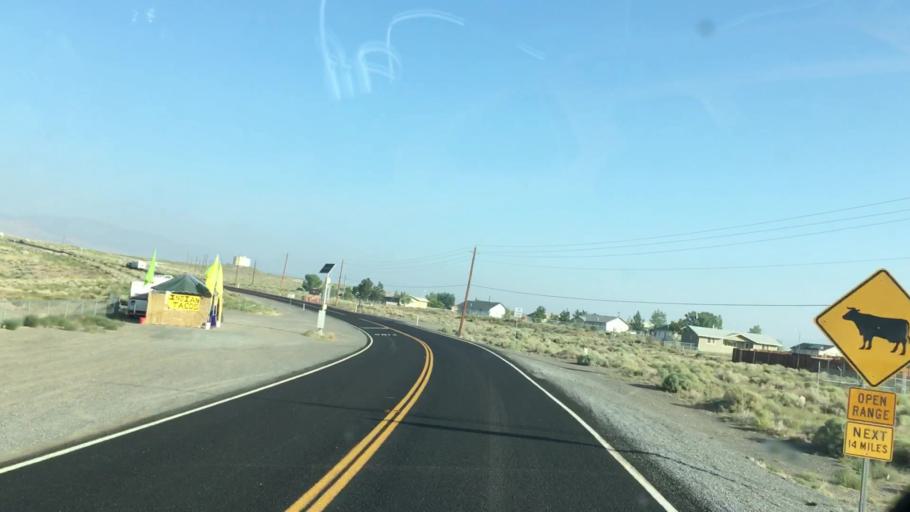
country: US
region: Nevada
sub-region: Lyon County
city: Fernley
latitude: 39.6369
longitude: -119.2909
